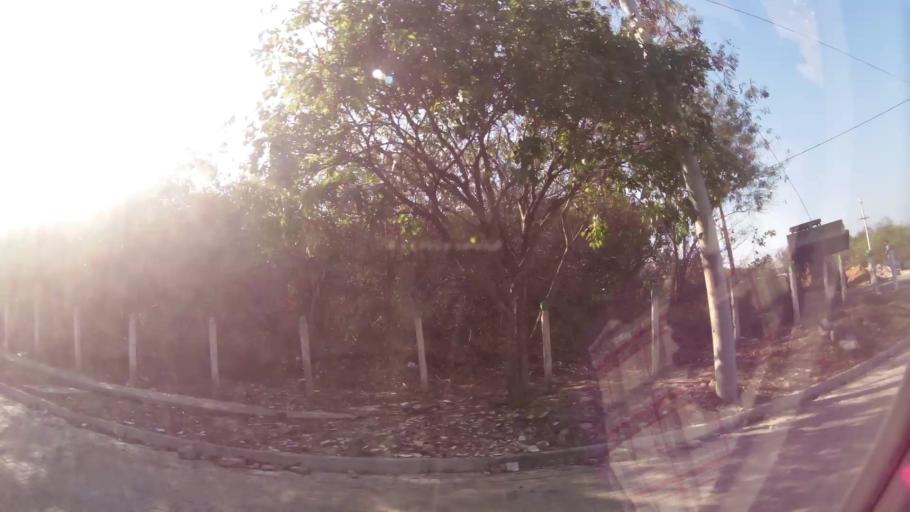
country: CO
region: Atlantico
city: Barranquilla
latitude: 11.0019
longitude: -74.8371
